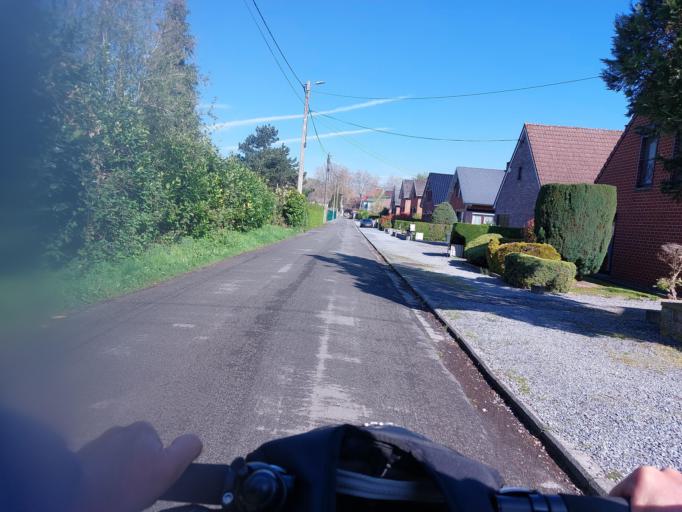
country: BE
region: Wallonia
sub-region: Province du Hainaut
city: Mons
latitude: 50.4512
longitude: 3.9684
